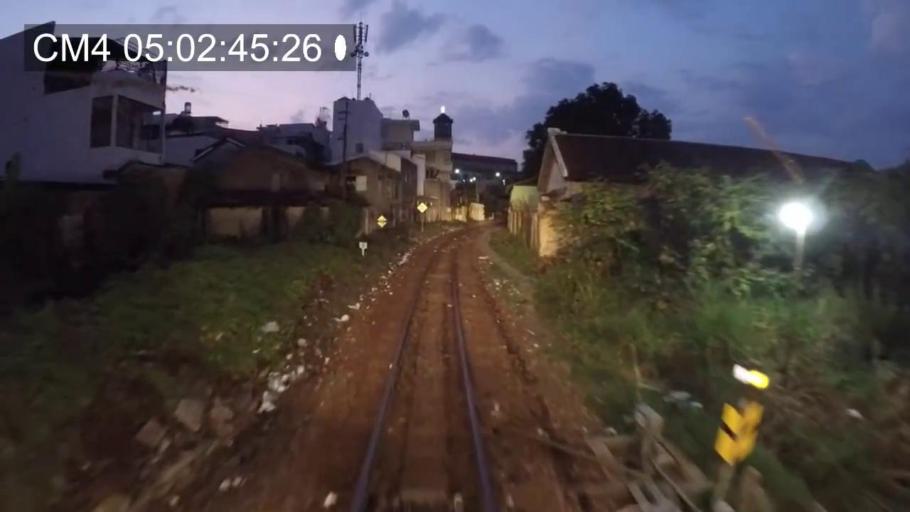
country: VN
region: Khanh Hoa
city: Nha Trang
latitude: 12.2517
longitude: 109.1735
